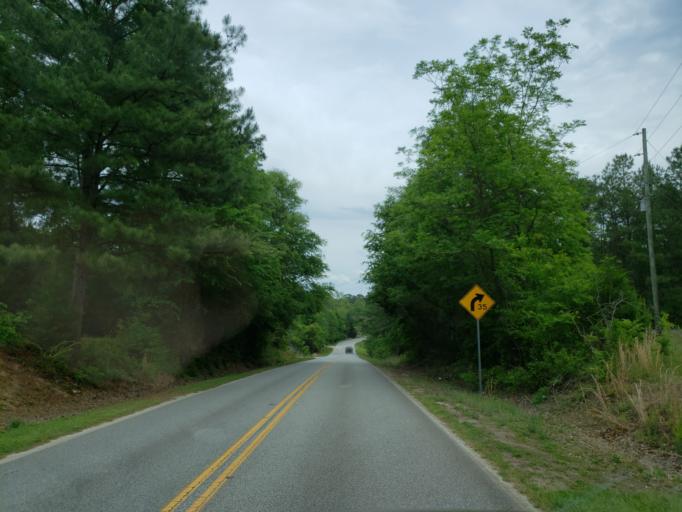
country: US
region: Georgia
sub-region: Bibb County
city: West Point
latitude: 32.8208
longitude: -83.8649
